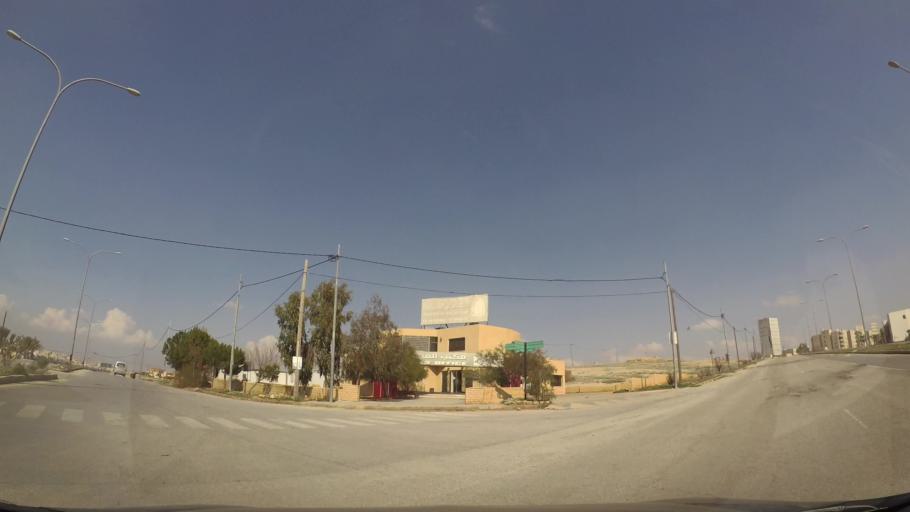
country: JO
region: Zarqa
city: Zarqa
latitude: 32.0726
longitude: 36.1072
